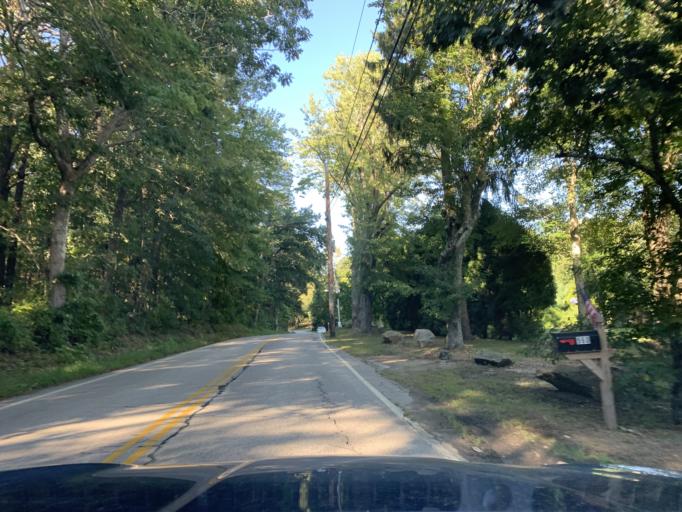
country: US
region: Rhode Island
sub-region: Washington County
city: North Kingstown
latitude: 41.5533
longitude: -71.4985
